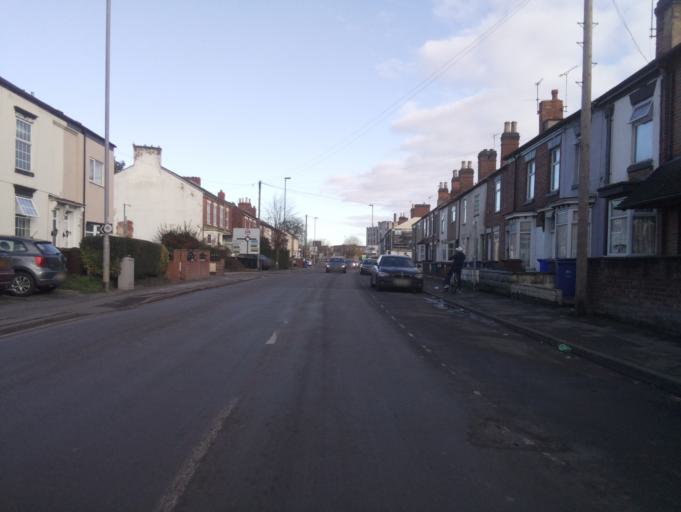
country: GB
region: England
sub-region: Staffordshire
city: Burton upon Trent
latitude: 52.7971
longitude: -1.6376
